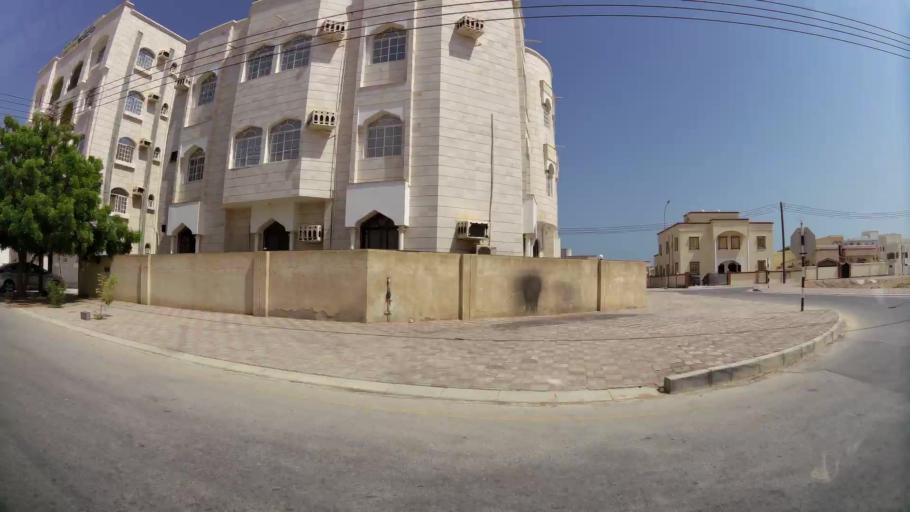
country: OM
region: Zufar
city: Salalah
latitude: 17.0202
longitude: 54.0705
